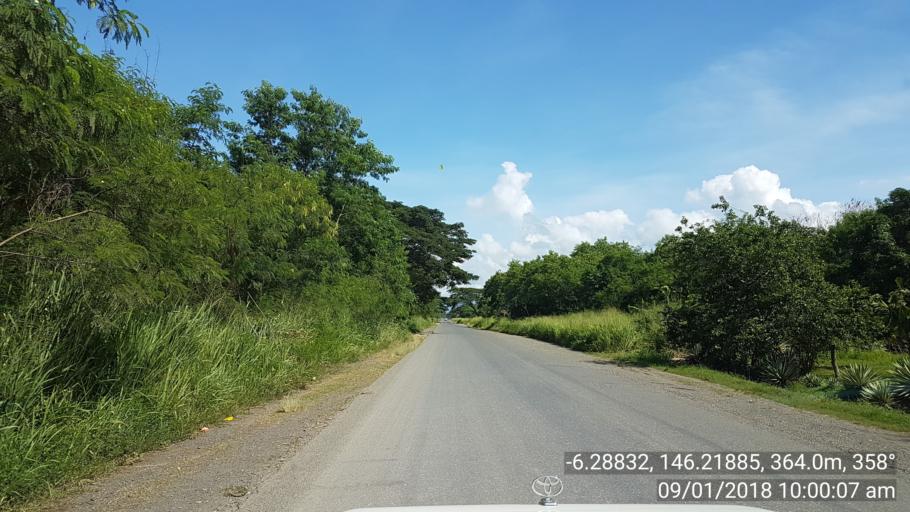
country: PG
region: Eastern Highlands
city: Kainantu
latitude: -6.2889
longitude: 146.2190
